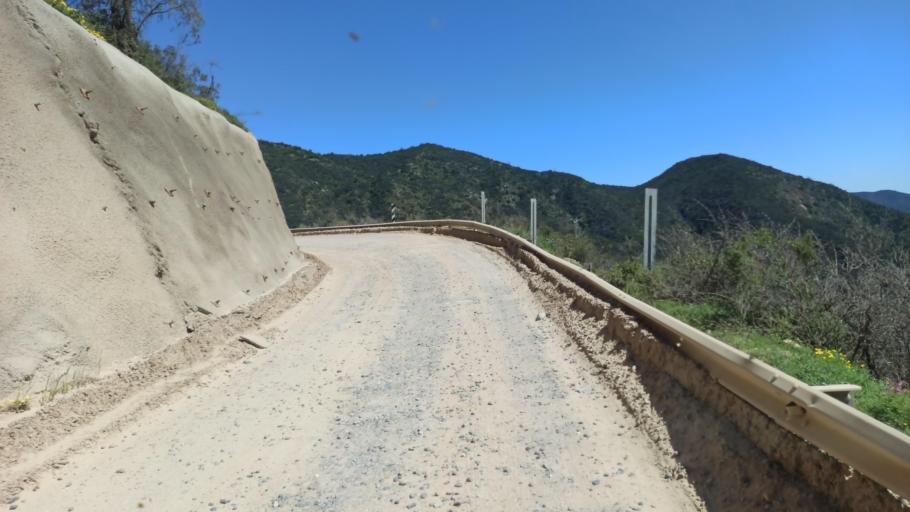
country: CL
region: Valparaiso
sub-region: Provincia de Marga Marga
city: Limache
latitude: -33.2052
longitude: -71.2586
